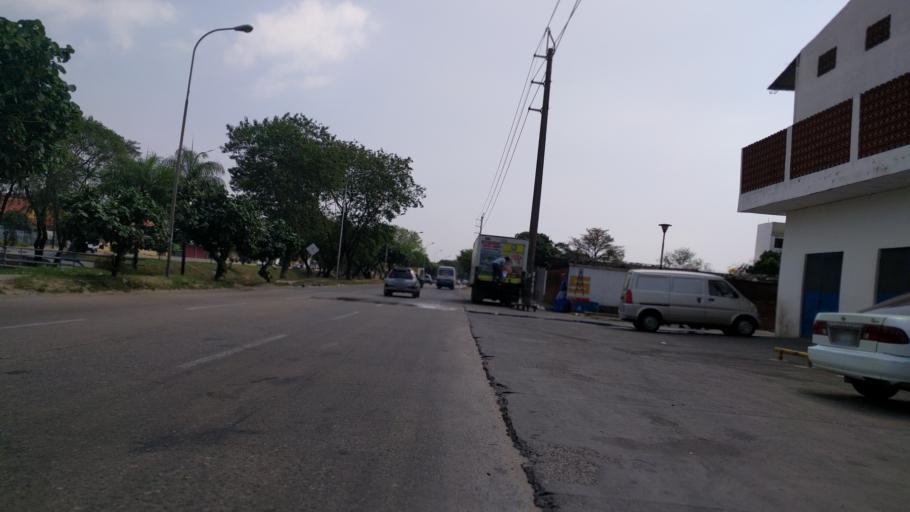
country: BO
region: Santa Cruz
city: Santa Cruz de la Sierra
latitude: -17.8106
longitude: -63.2090
